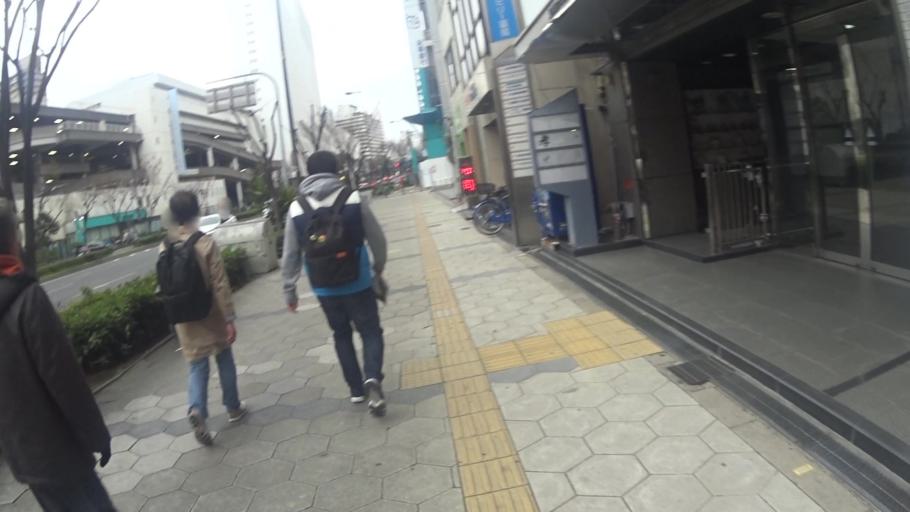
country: JP
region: Osaka
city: Osaka-shi
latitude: 34.6663
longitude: 135.5231
